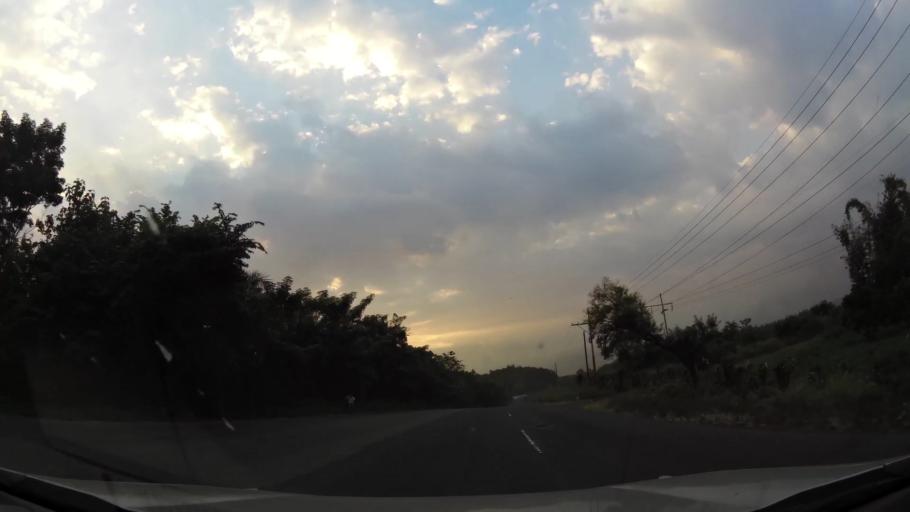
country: GT
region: Escuintla
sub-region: Municipio de La Democracia
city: La Democracia
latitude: 14.2713
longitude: -90.9026
